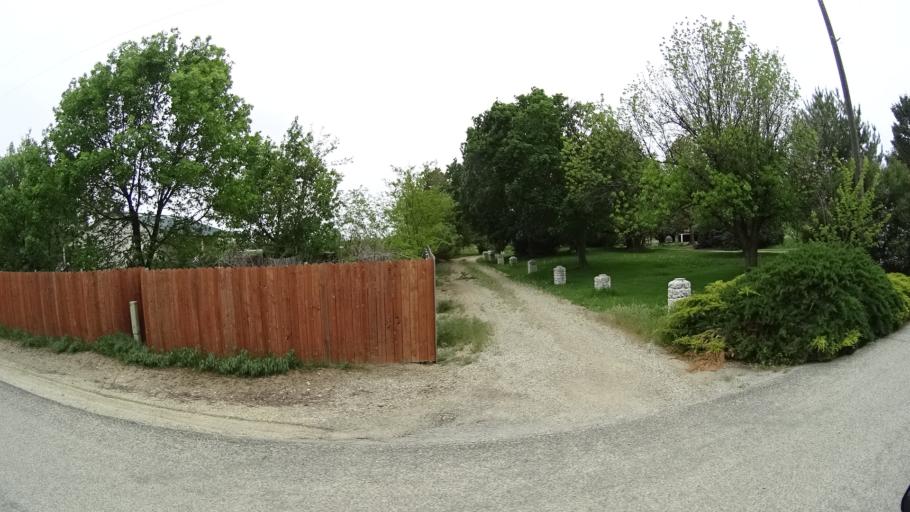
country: US
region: Idaho
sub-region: Ada County
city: Kuna
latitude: 43.4937
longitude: -116.3380
